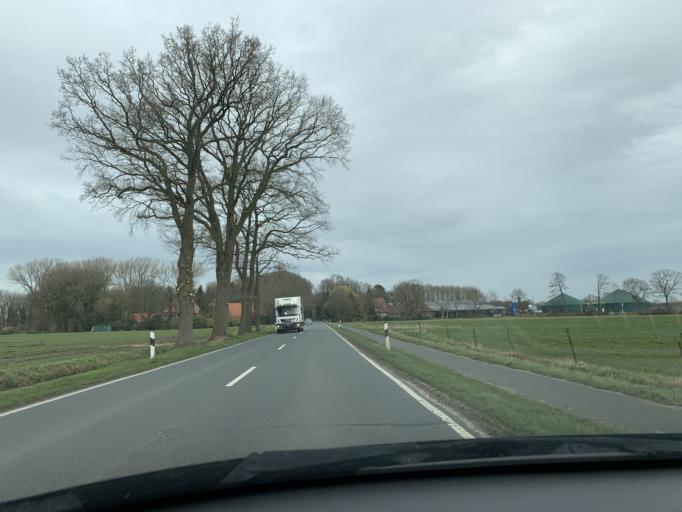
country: DE
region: Lower Saxony
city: Bad Zwischenahn
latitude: 53.1643
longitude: 7.9673
